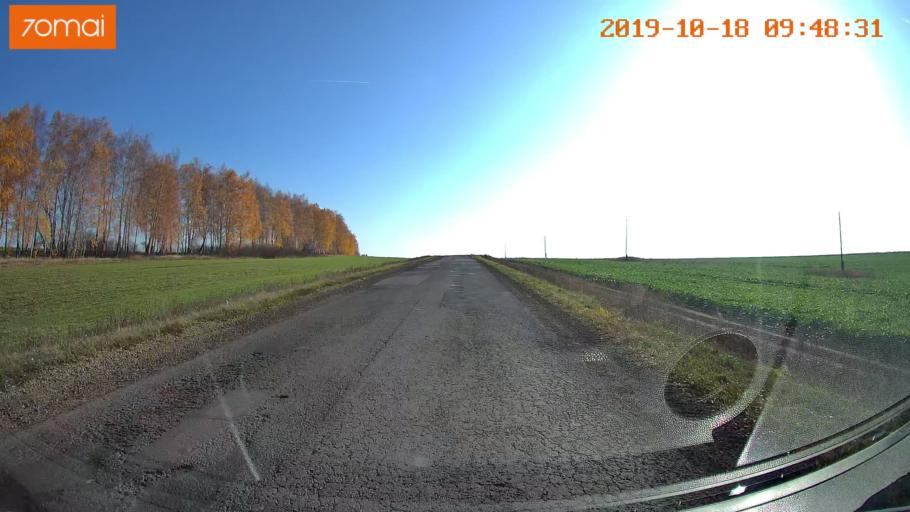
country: RU
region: Tula
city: Kazachka
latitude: 53.3176
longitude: 38.2513
